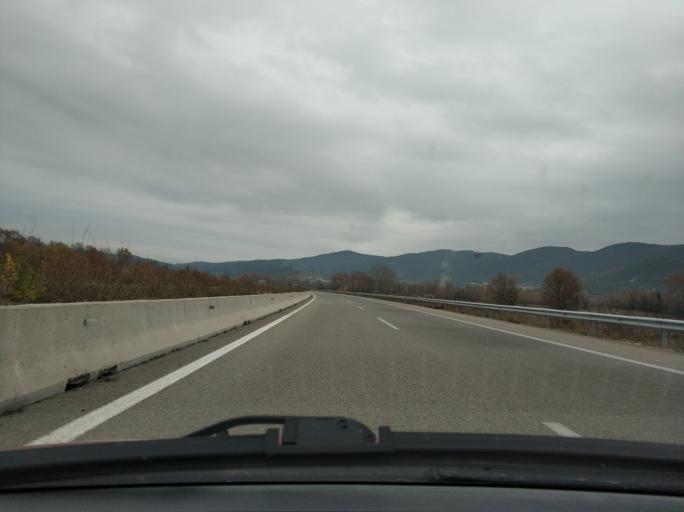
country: GR
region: East Macedonia and Thrace
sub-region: Nomos Kavalas
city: Eleftheres
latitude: 40.8786
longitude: 24.2185
